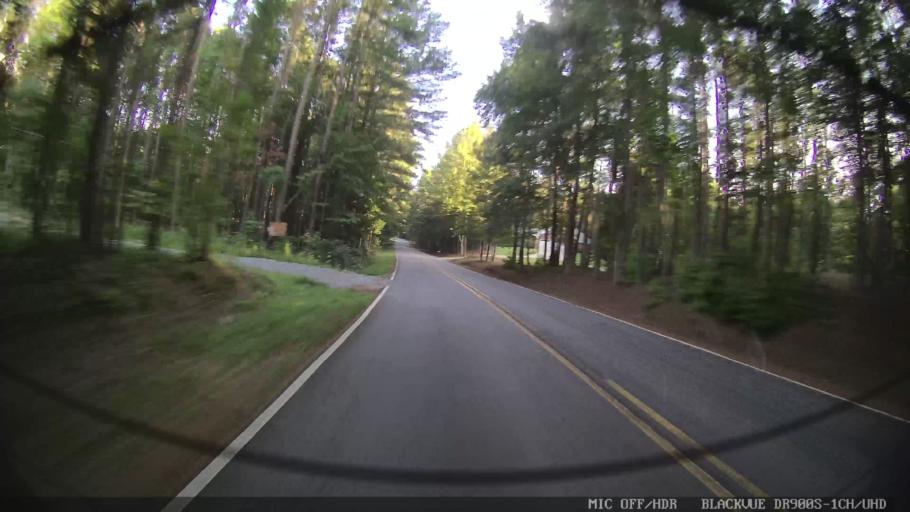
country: US
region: Georgia
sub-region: Bartow County
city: Emerson
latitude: 34.2152
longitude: -84.6948
